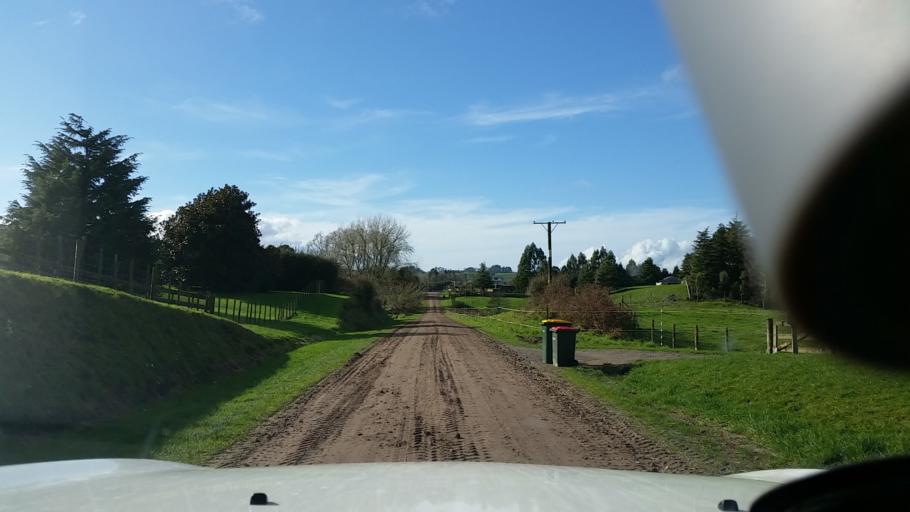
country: NZ
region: Bay of Plenty
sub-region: Rotorua District
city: Rotorua
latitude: -38.0373
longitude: 176.1950
